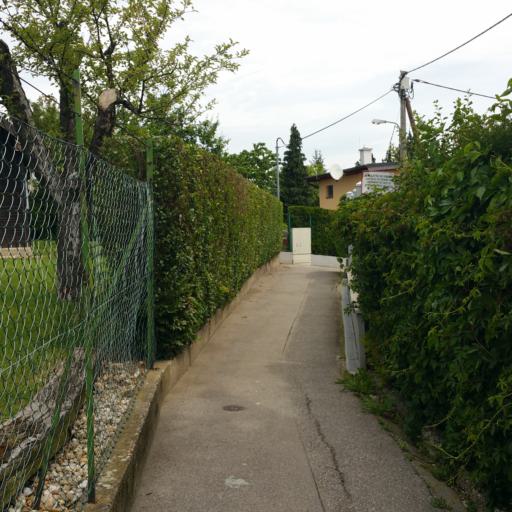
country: AT
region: Vienna
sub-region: Wien Stadt
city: Vienna
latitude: 48.2093
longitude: 16.2954
